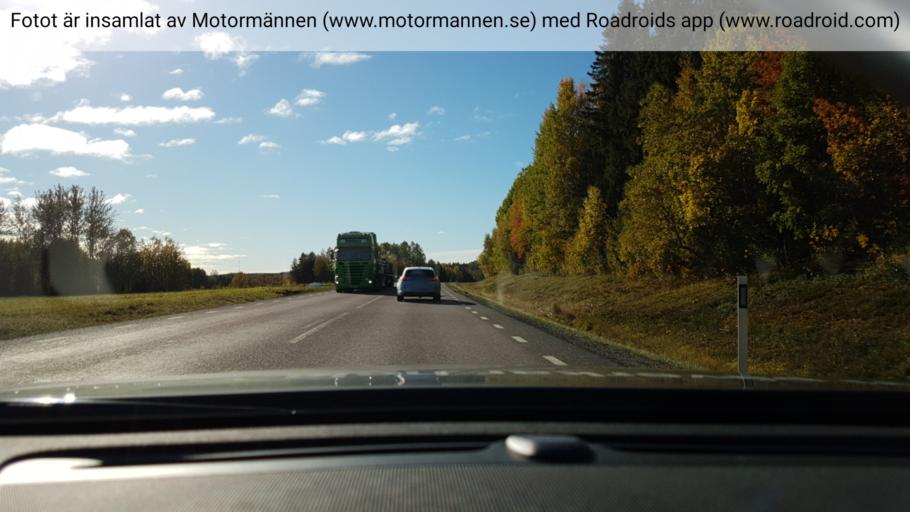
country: SE
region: Vaesterbotten
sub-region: Skelleftea Kommun
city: Burea
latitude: 64.4000
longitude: 21.3011
